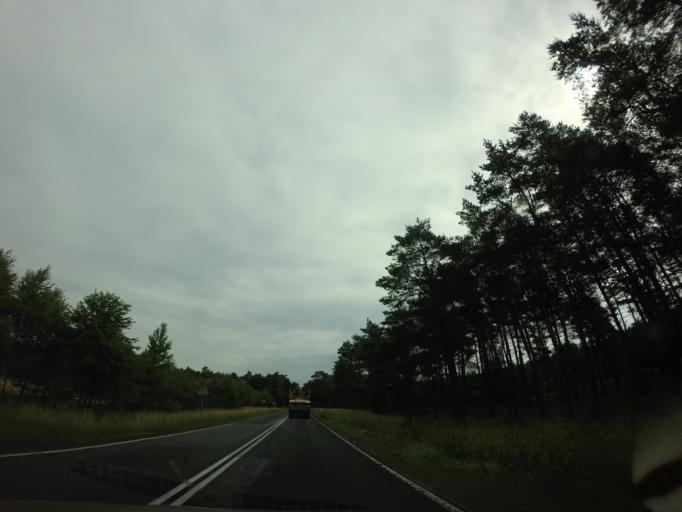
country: PL
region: West Pomeranian Voivodeship
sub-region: Powiat drawski
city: Kalisz Pomorski
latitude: 53.3113
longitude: 15.9928
